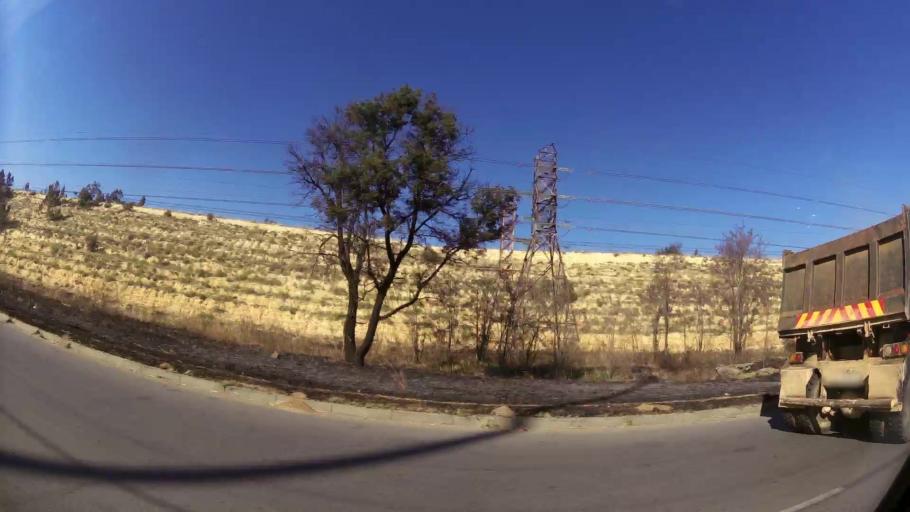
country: ZA
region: Gauteng
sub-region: City of Johannesburg Metropolitan Municipality
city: Johannesburg
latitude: -26.2284
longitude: 28.0984
